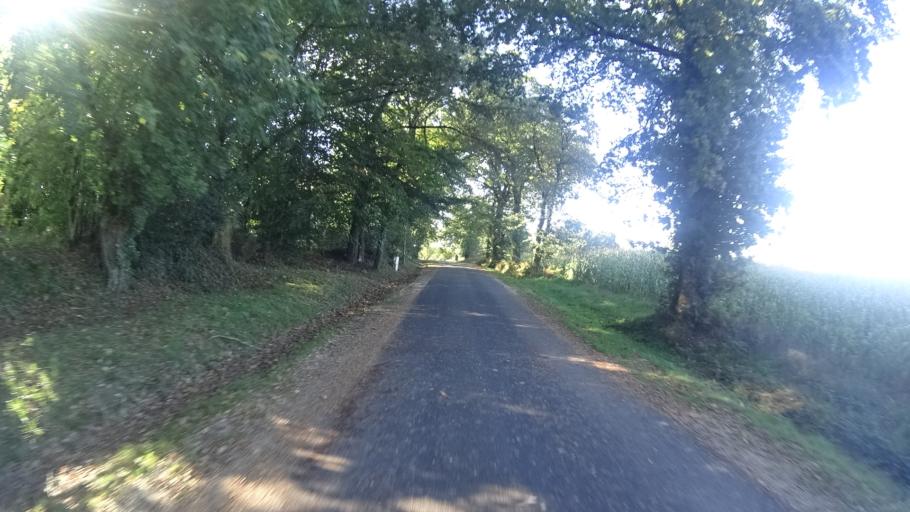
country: FR
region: Brittany
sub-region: Departement du Morbihan
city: Peillac
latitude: 47.7106
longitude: -2.1975
